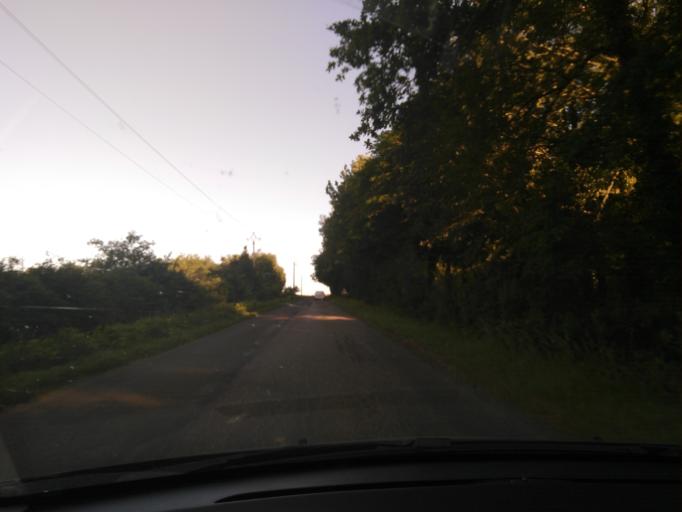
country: FR
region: Midi-Pyrenees
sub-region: Departement du Gers
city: Valence-sur-Baise
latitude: 43.8917
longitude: 0.3635
